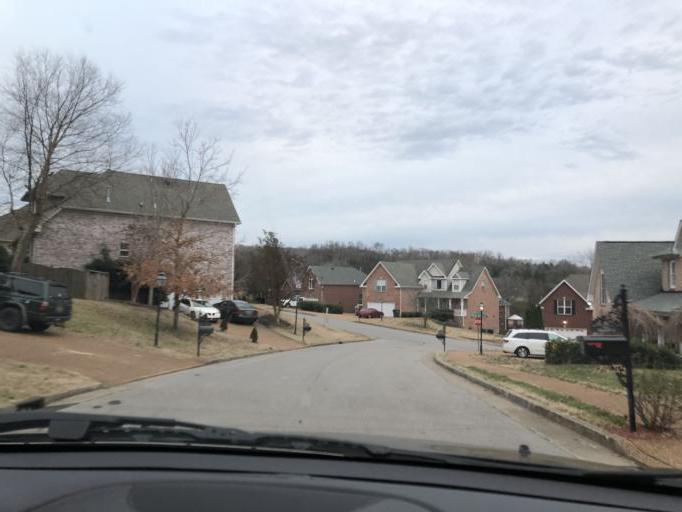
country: US
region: Tennessee
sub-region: Wilson County
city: Green Hill
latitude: 36.1966
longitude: -86.5919
